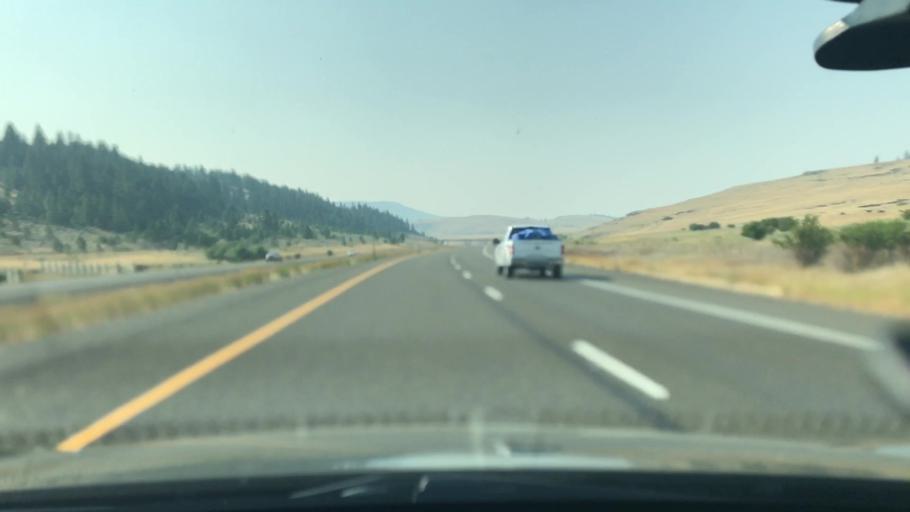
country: US
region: Oregon
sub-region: Union County
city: Union
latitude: 45.1757
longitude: -117.9792
